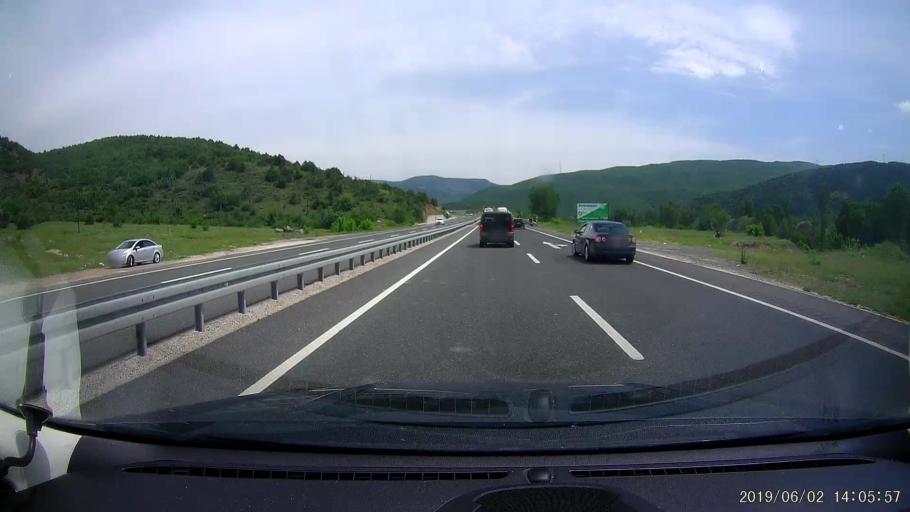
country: TR
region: Cankiri
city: Ilgaz
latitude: 40.8948
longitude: 33.6755
